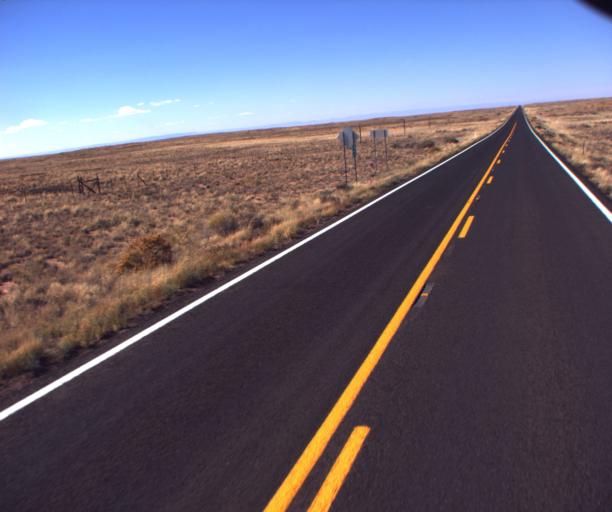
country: US
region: Arizona
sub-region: Coconino County
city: Tuba City
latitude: 35.9612
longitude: -110.9399
